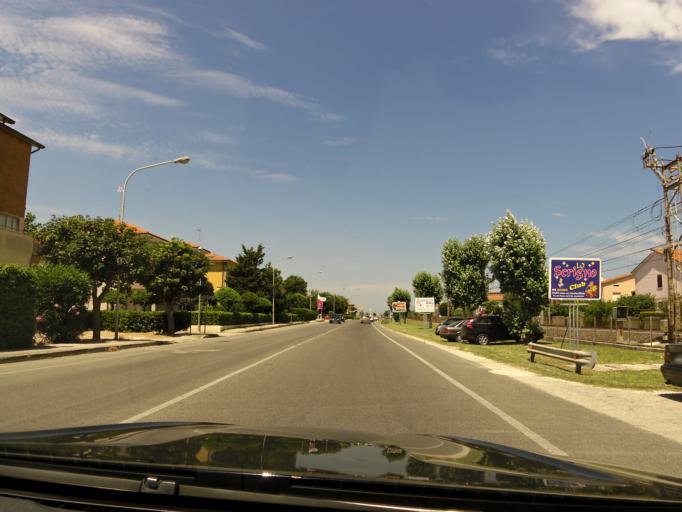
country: IT
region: The Marches
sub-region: Provincia di Pesaro e Urbino
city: Marotta
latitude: 43.7748
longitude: 13.1285
